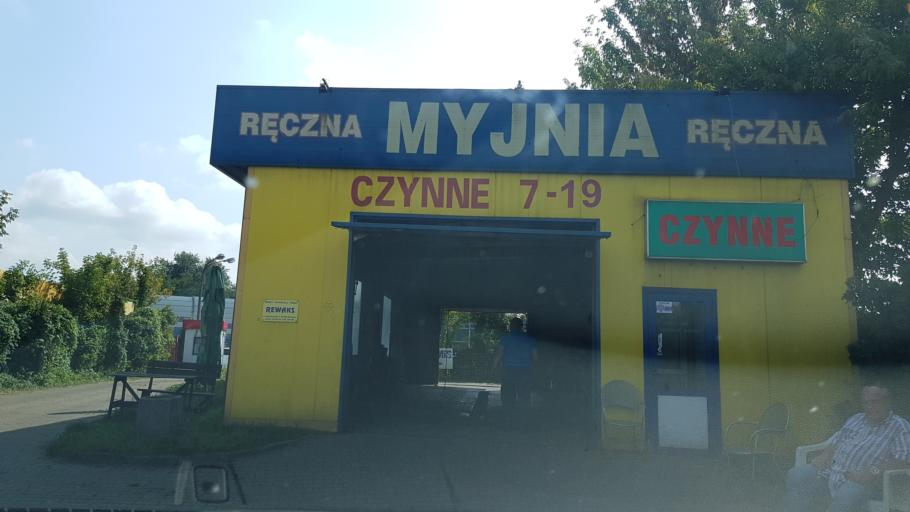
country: PL
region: Masovian Voivodeship
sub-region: Warszawa
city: Zoliborz
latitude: 52.2786
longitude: 20.9745
